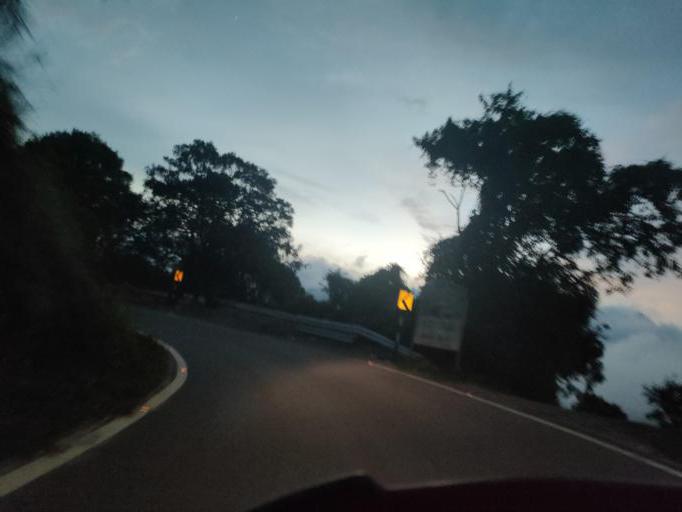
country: IN
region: Tamil Nadu
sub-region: Dindigul
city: Kodaikanal
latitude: 10.2813
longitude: 77.5328
